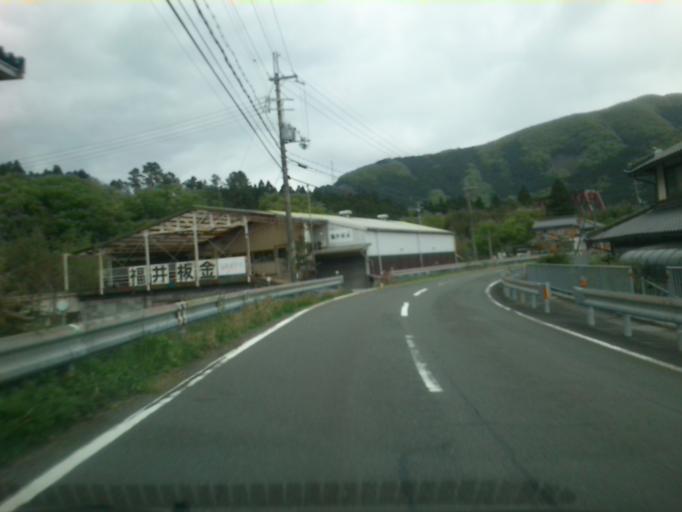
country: JP
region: Kyoto
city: Ayabe
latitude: 35.2618
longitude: 135.3963
